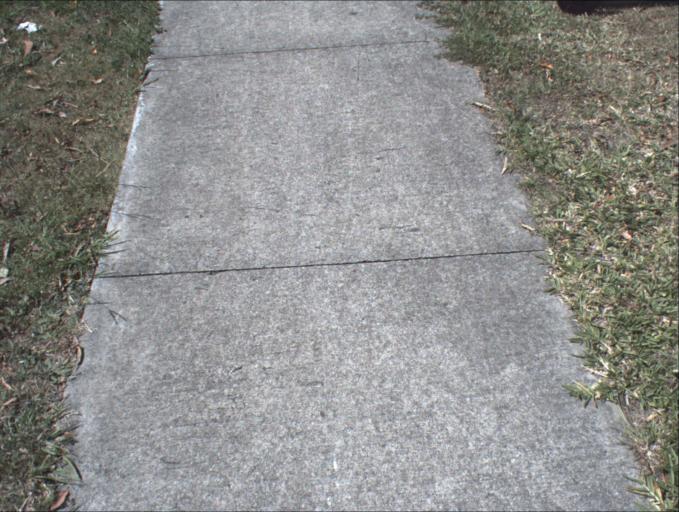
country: AU
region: Queensland
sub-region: Gold Coast
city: Yatala
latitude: -27.6951
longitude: 153.2187
